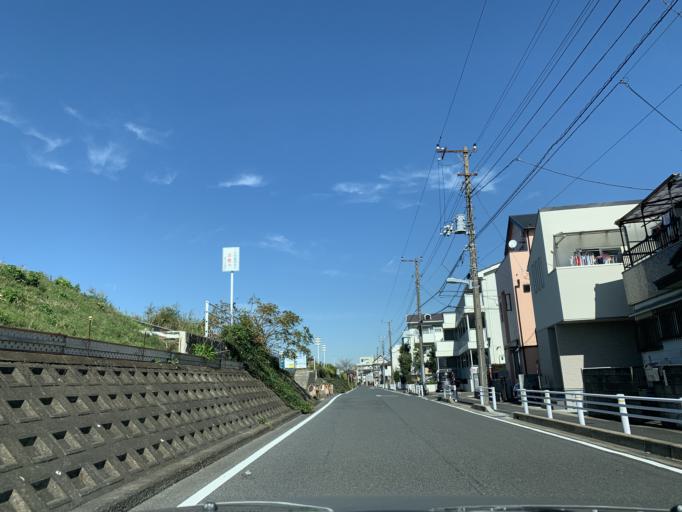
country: JP
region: Tokyo
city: Urayasu
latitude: 35.6524
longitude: 139.8876
